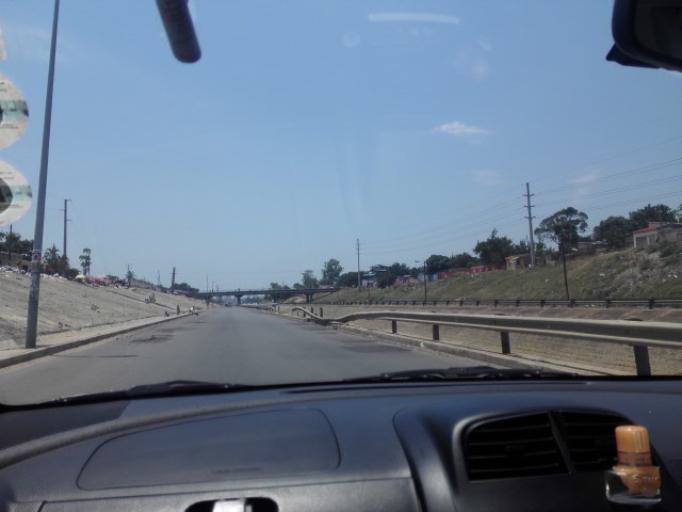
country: MZ
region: Maputo City
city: Maputo
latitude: -25.9320
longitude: 32.5599
